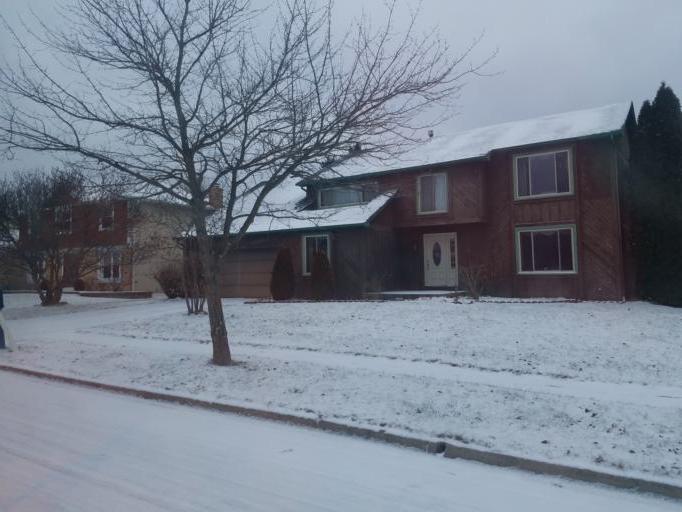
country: US
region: Ohio
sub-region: Delaware County
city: Powell
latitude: 40.1254
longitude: -83.0758
